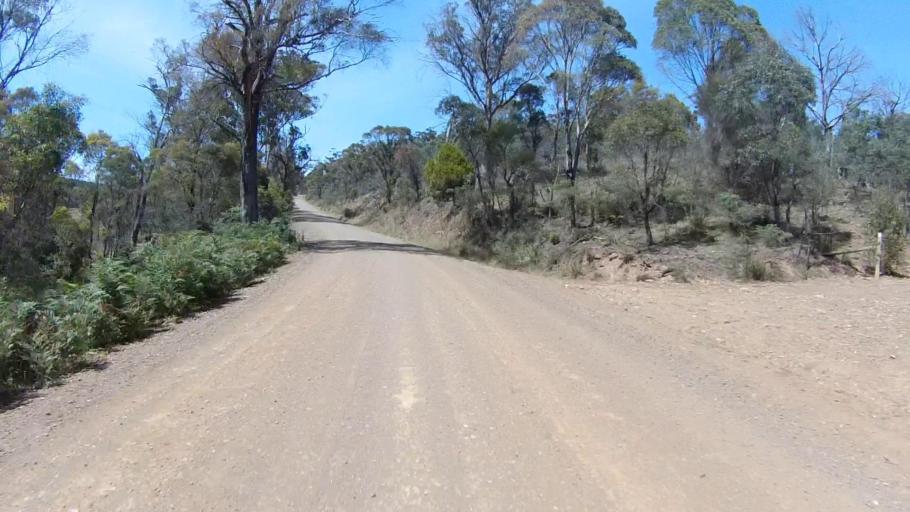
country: AU
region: Tasmania
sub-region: Sorell
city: Sorell
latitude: -42.6448
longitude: 147.7413
